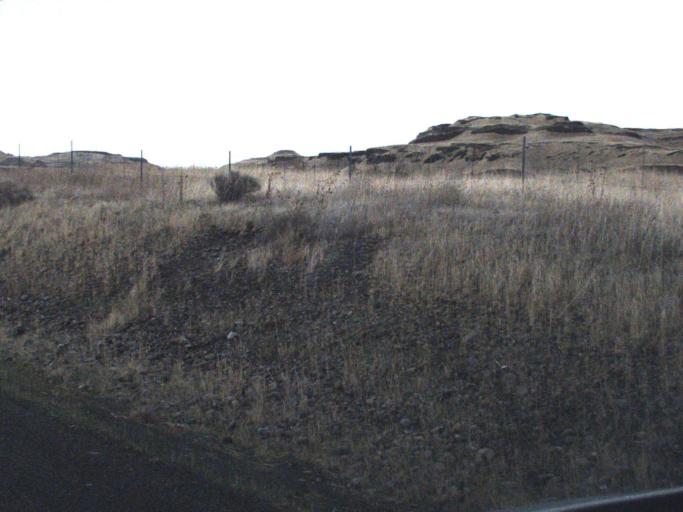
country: US
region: Washington
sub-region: Walla Walla County
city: Waitsburg
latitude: 46.5768
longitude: -118.2090
